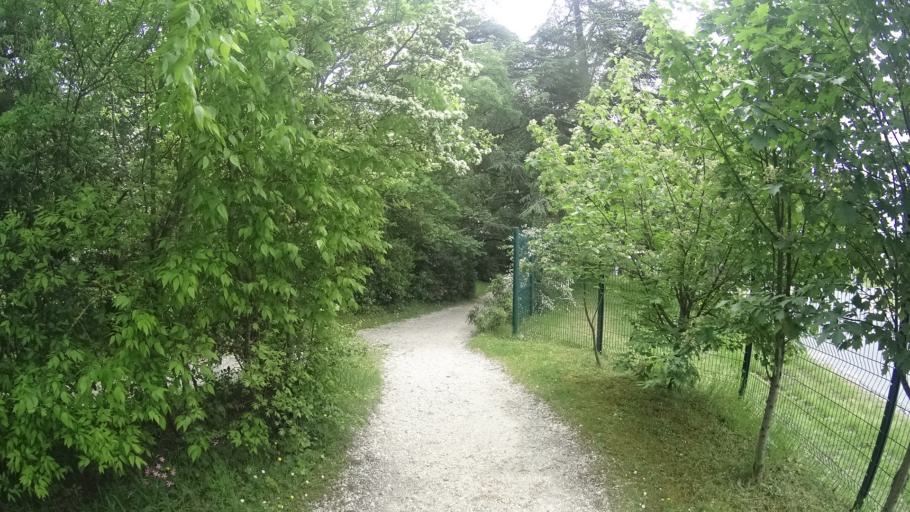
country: FR
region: Aquitaine
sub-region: Departement de la Gironde
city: Talence
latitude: 44.7890
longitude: -0.5842
